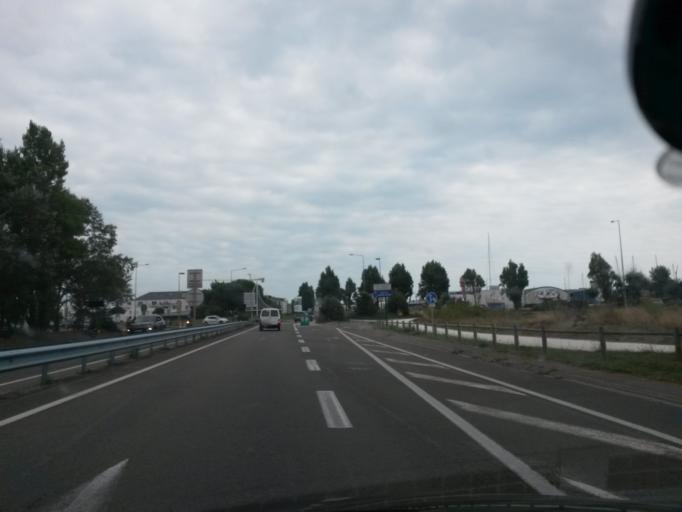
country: FR
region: Pays de la Loire
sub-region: Departement de la Vendee
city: Les Sables-d'Olonne
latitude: 46.5060
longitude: -1.7906
